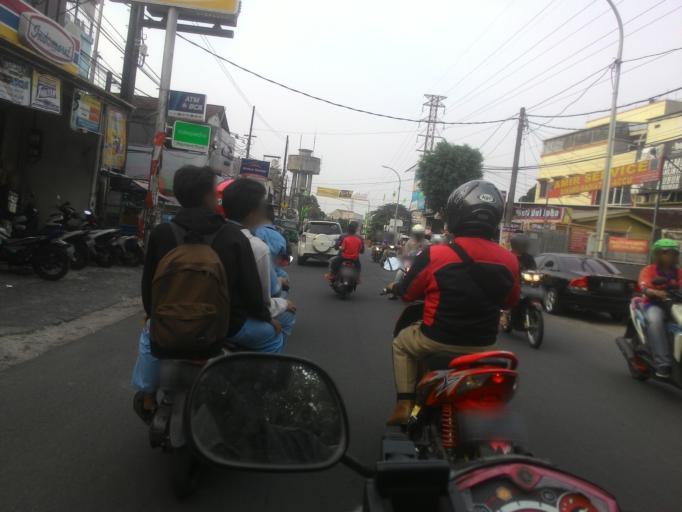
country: ID
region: West Java
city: Depok
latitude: -6.3864
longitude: 106.8144
